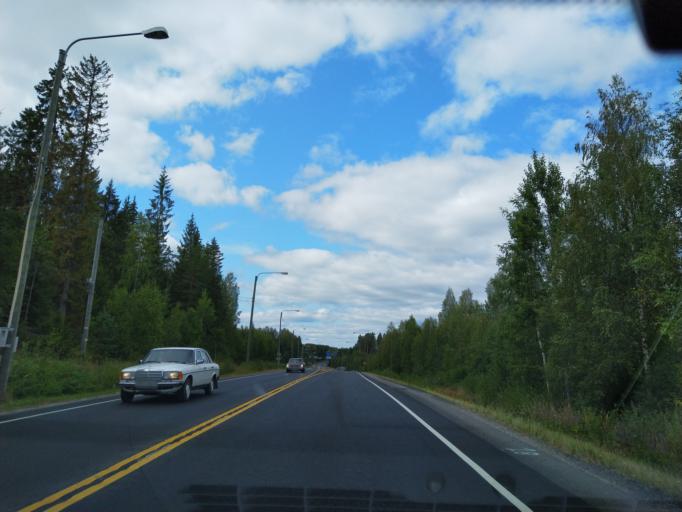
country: FI
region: Haeme
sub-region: Riihimaeki
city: Loppi
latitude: 60.7214
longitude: 24.4494
